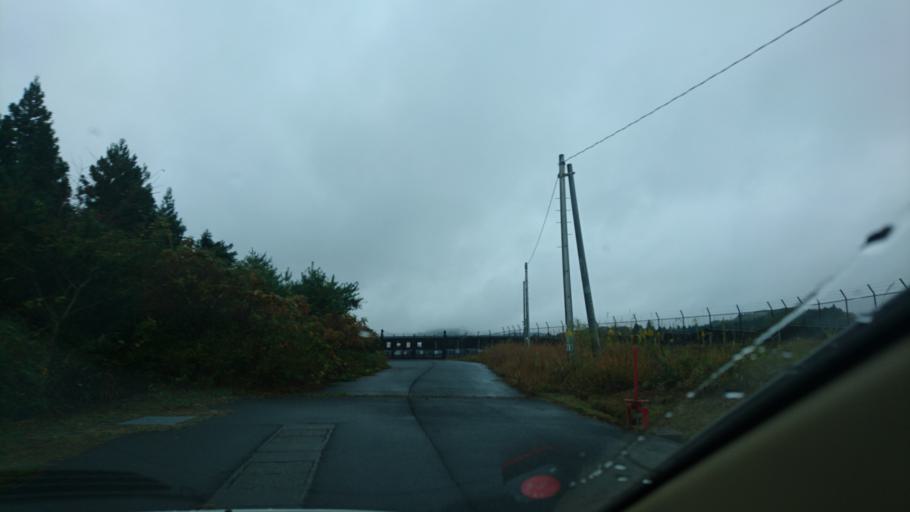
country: JP
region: Iwate
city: Ichinoseki
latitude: 38.9680
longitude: 141.1026
